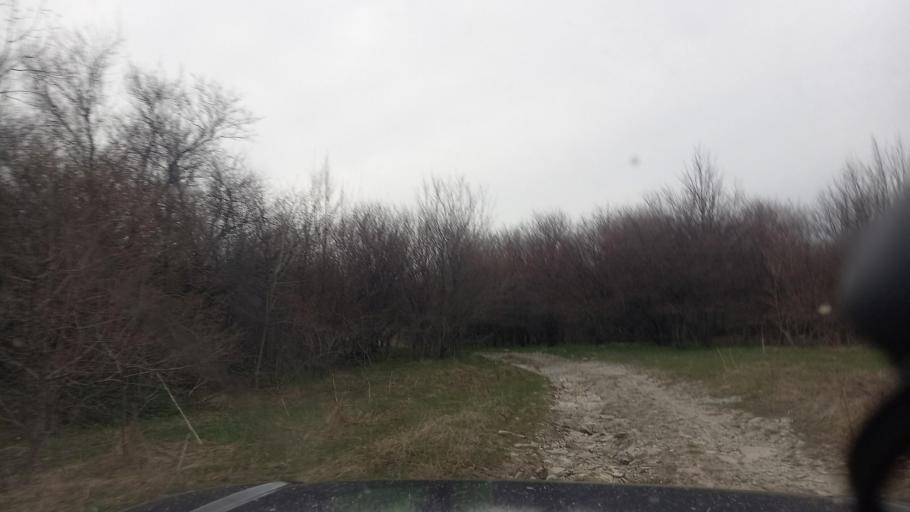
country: RU
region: Krasnodarskiy
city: Pshada
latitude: 44.5988
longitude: 38.2811
